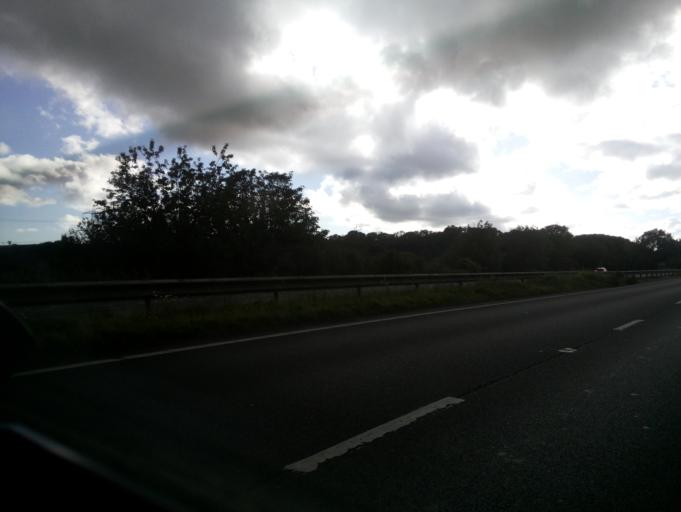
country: GB
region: England
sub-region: Devon
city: Ivybridge
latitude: 50.3850
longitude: -3.9185
